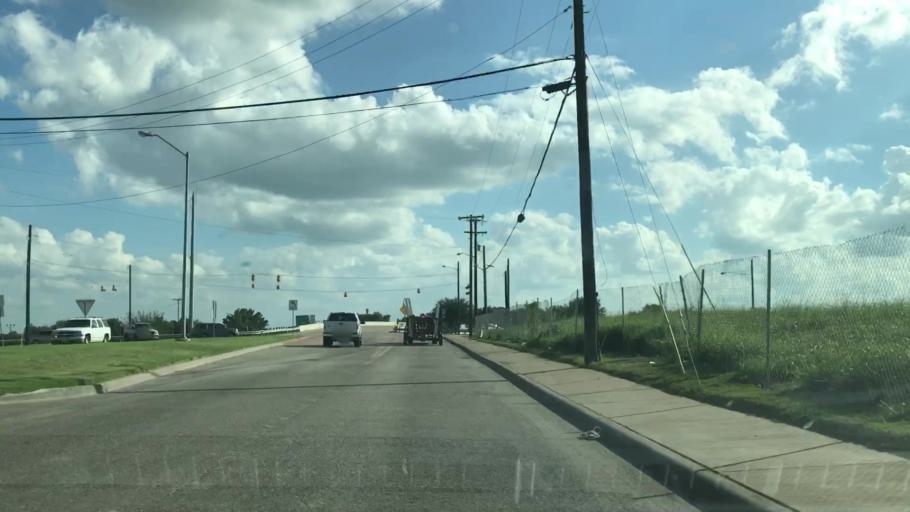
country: US
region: Texas
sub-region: Dallas County
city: Rowlett
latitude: 32.8781
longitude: -96.5184
